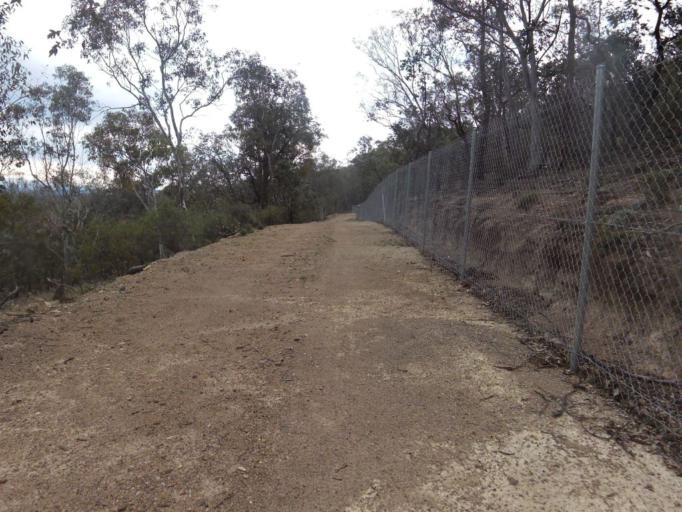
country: AU
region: Australian Capital Territory
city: Forrest
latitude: -35.3523
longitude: 149.1241
